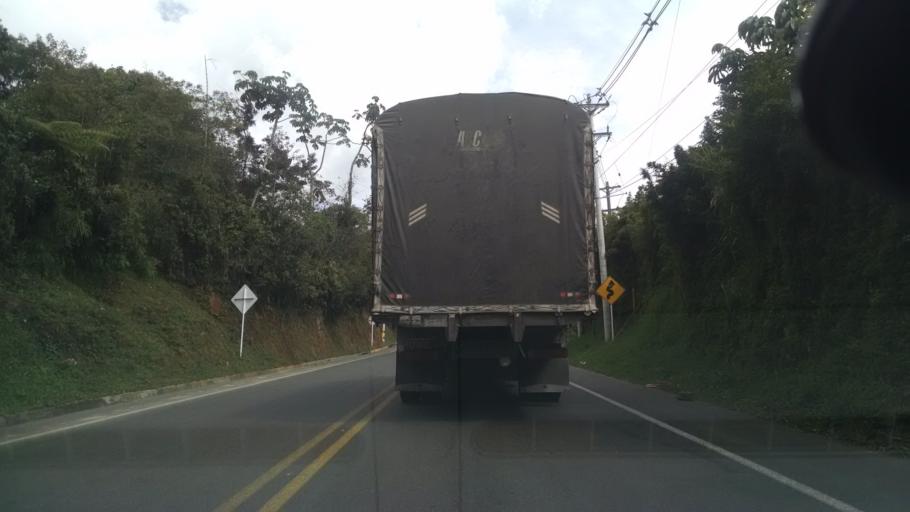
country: CO
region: Antioquia
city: Caldas
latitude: 6.0342
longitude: -75.6251
